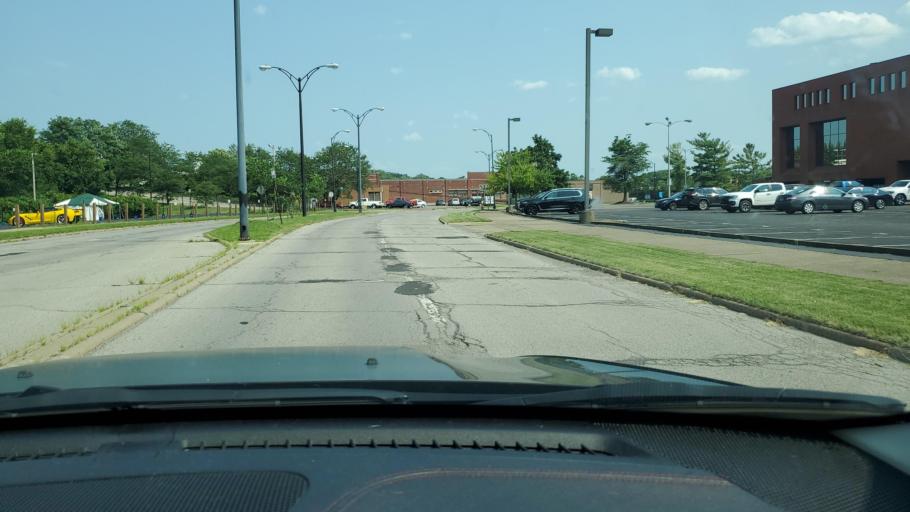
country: US
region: Ohio
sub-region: Mahoning County
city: Youngstown
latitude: 41.0999
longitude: -80.6461
